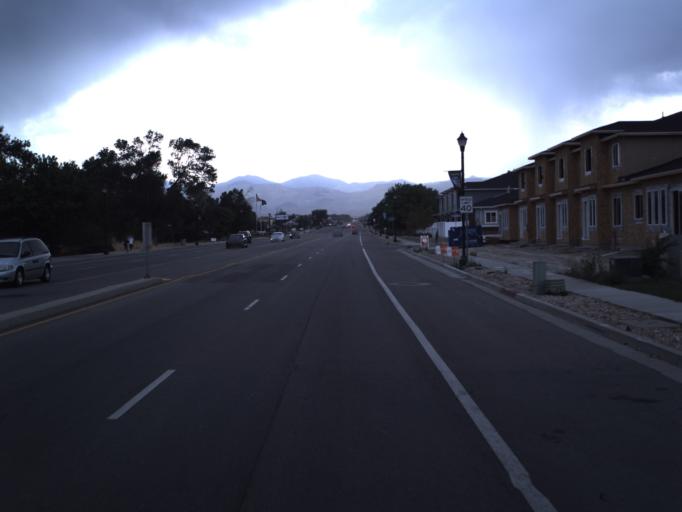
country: US
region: Utah
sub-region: Salt Lake County
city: Riverton
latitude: 40.5224
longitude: -111.9299
